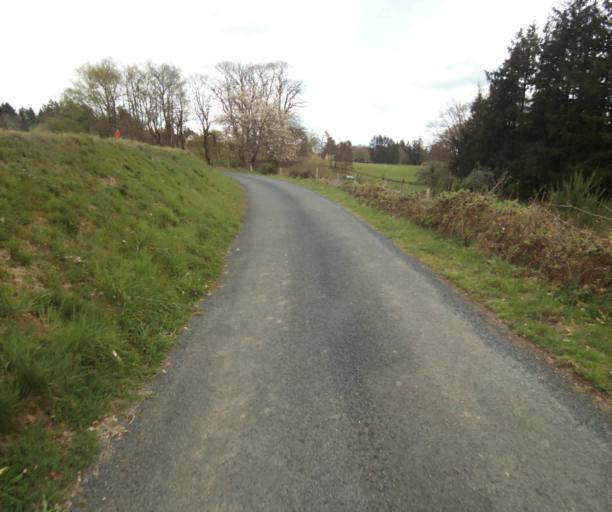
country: FR
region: Limousin
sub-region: Departement de la Correze
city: Laguenne
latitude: 45.2083
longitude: 1.8732
